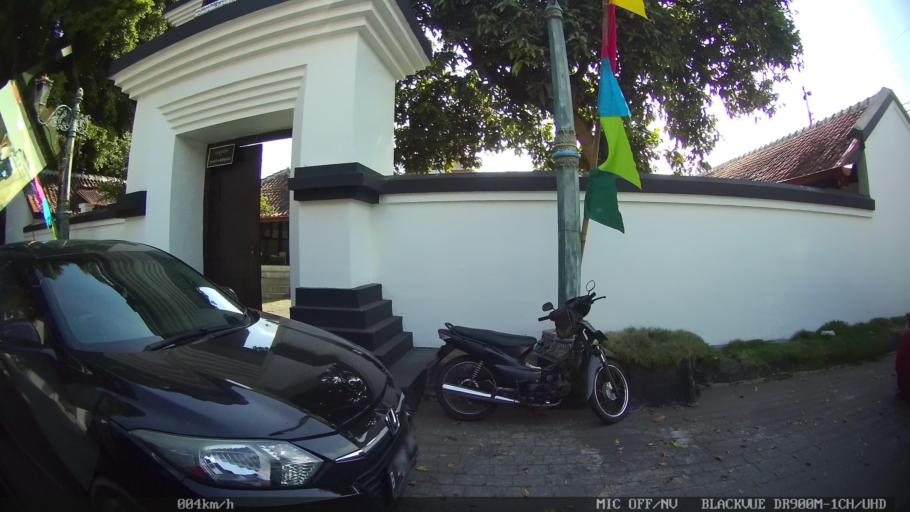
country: ID
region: Daerah Istimewa Yogyakarta
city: Sewon
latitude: -7.8318
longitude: 110.3992
